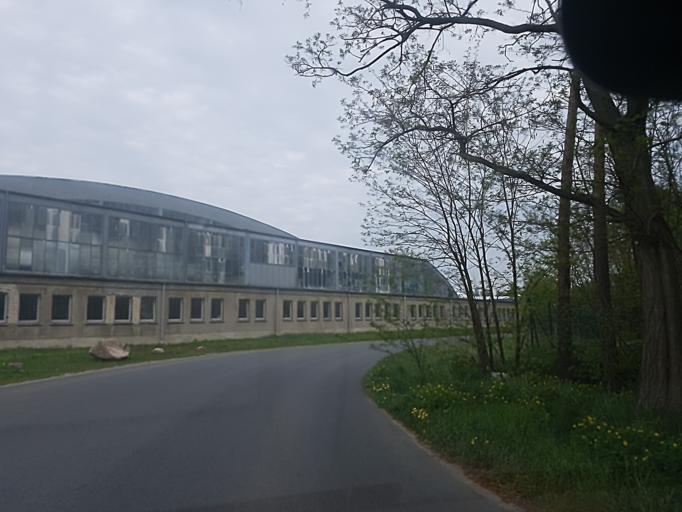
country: DE
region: Brandenburg
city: Finsterwalde
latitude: 51.6014
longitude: 13.7414
